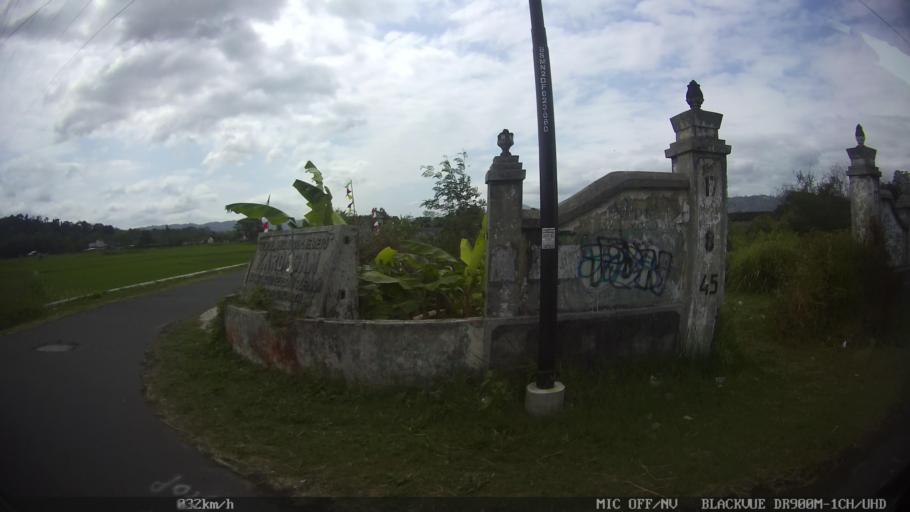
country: ID
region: Daerah Istimewa Yogyakarta
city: Depok
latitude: -7.8157
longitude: 110.4651
